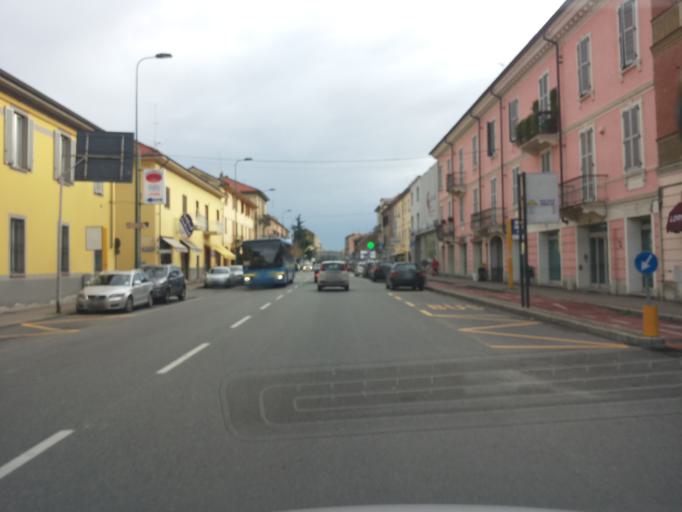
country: IT
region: Piedmont
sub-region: Provincia di Alessandria
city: Casale Monferrato
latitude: 45.1269
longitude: 8.4508
